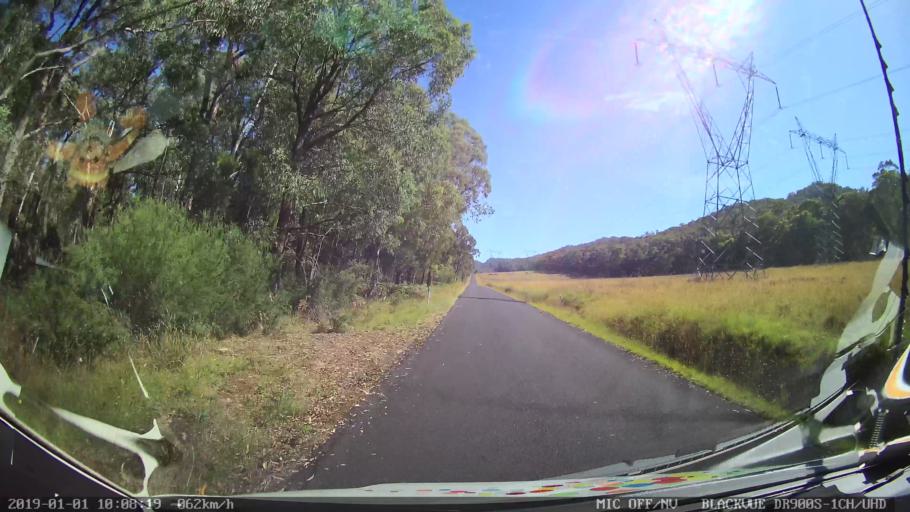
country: AU
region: New South Wales
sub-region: Snowy River
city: Jindabyne
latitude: -36.1607
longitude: 148.1575
